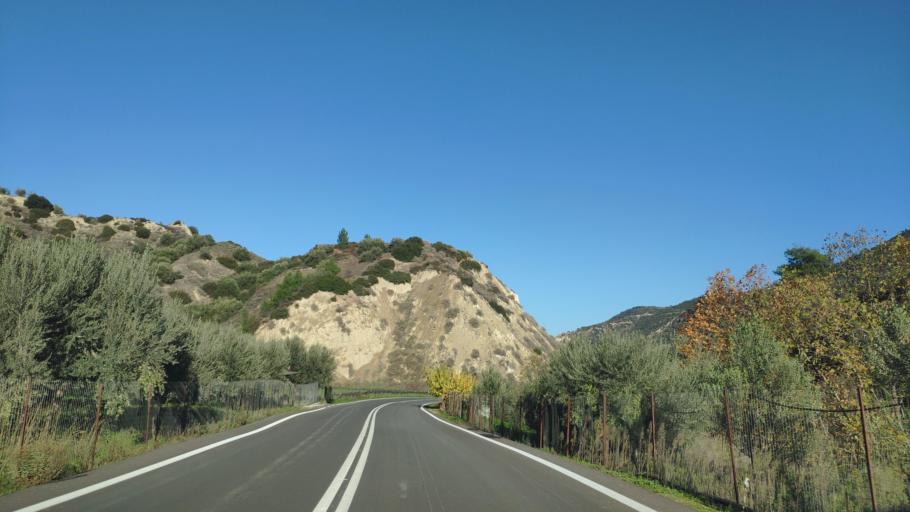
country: GR
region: Peloponnese
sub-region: Nomos Korinthias
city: Xylokastro
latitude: 38.0139
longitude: 22.5470
